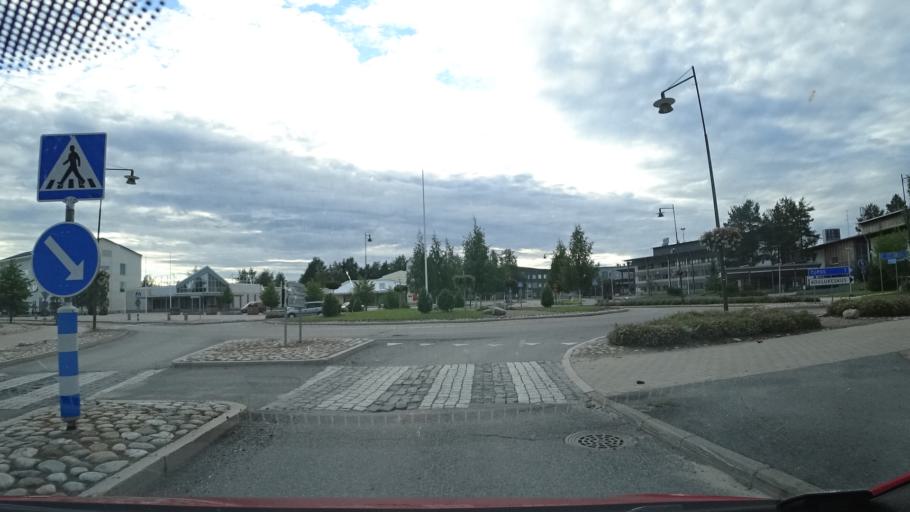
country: FI
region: Northern Ostrobothnia
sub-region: Oulu
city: Liminka
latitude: 64.8097
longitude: 25.4162
